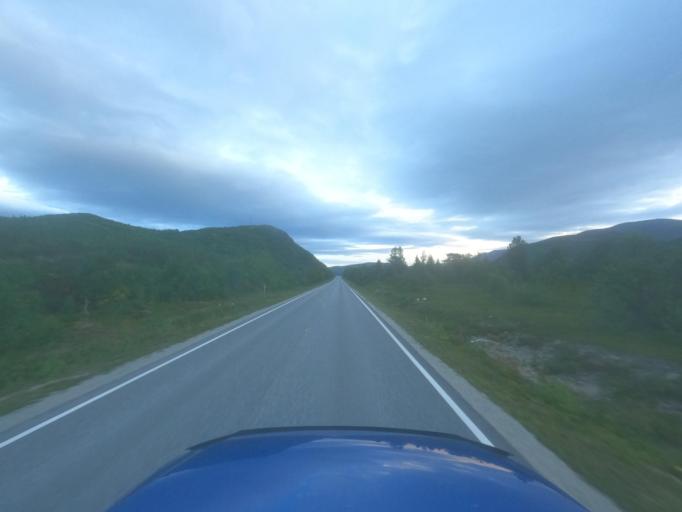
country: NO
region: Finnmark Fylke
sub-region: Porsanger
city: Lakselv
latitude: 69.9245
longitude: 24.9820
